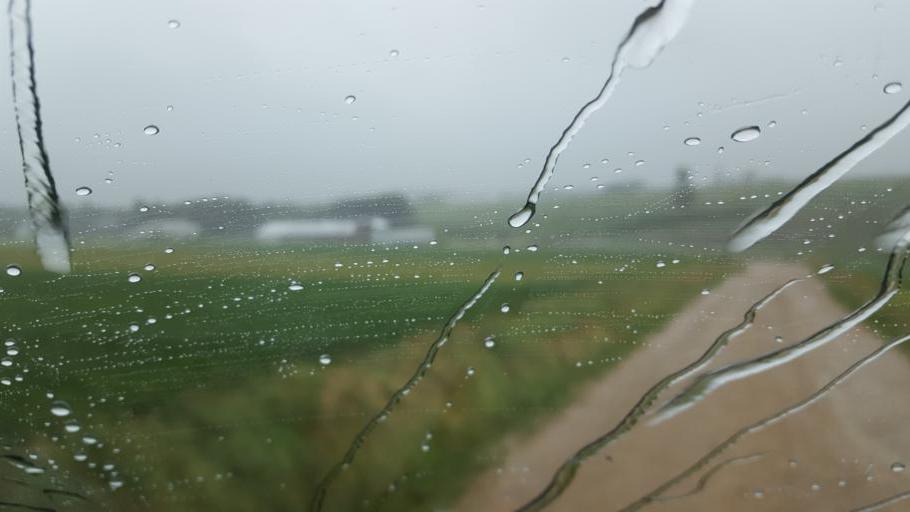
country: US
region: Wisconsin
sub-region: Vernon County
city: Hillsboro
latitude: 43.6223
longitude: -90.4485
